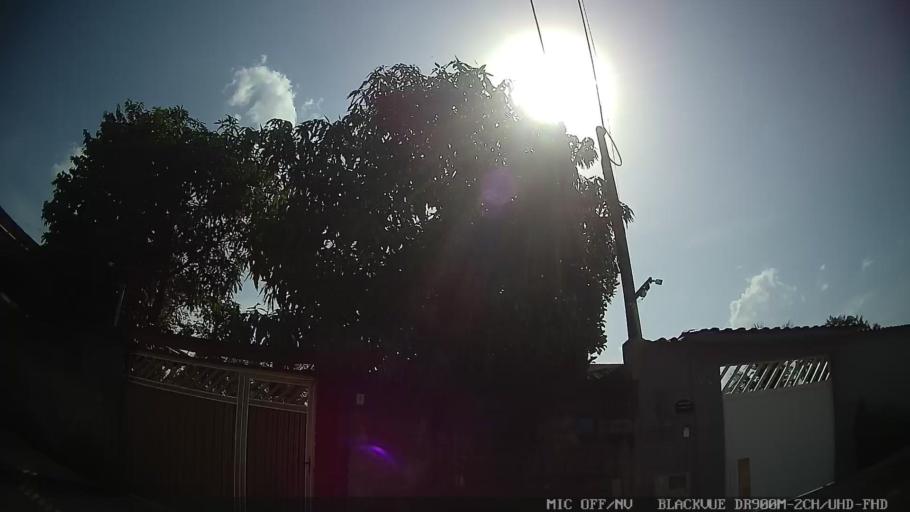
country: BR
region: Sao Paulo
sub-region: Guaruja
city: Guaruja
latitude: -23.9753
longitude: -46.2013
